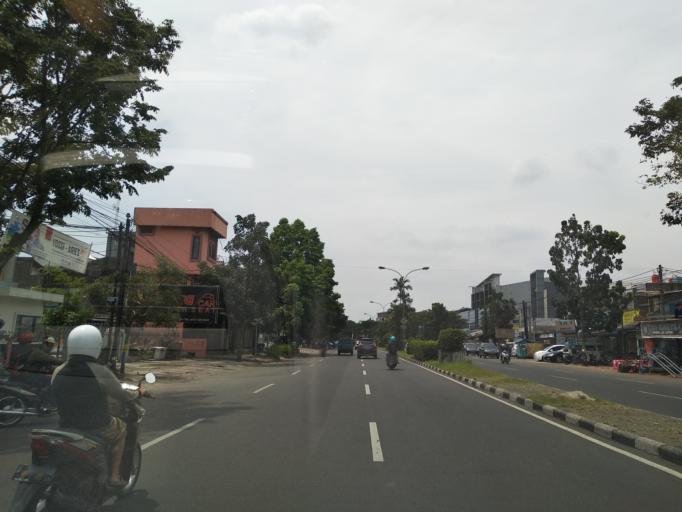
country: ID
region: West Java
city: Bandung
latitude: -6.9380
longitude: 107.6180
